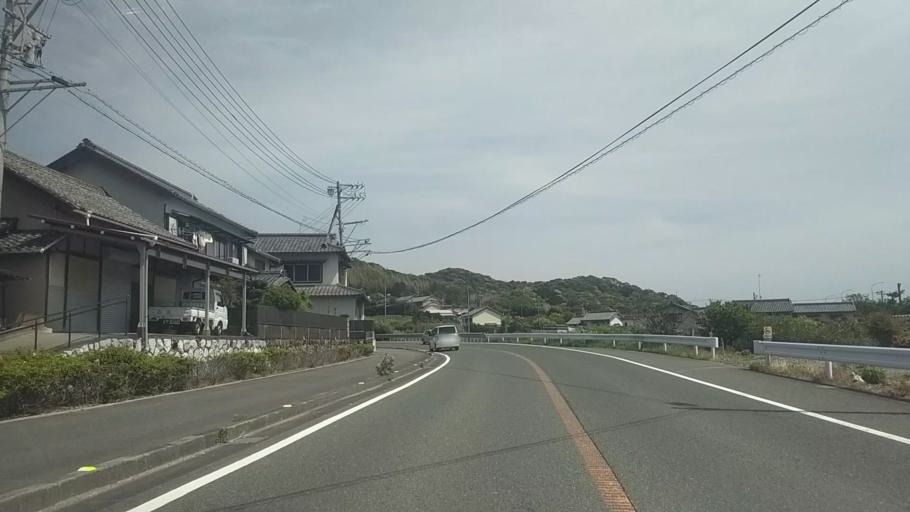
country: JP
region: Shizuoka
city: Kosai-shi
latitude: 34.7884
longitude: 137.6048
